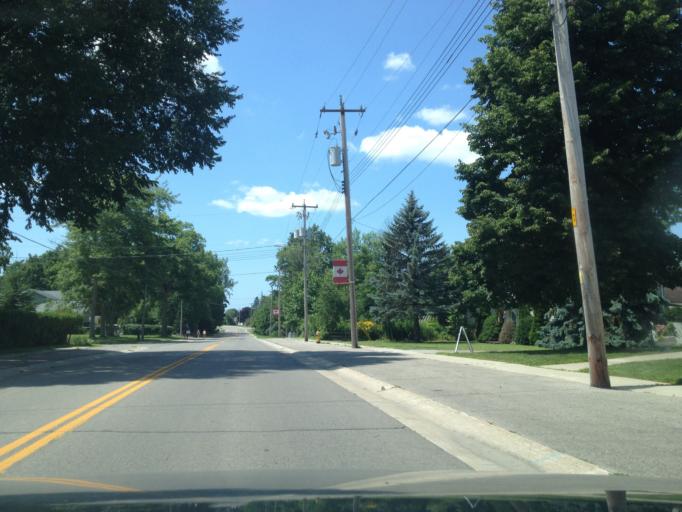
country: CA
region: Ontario
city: Norfolk County
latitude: 42.6206
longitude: -80.4529
